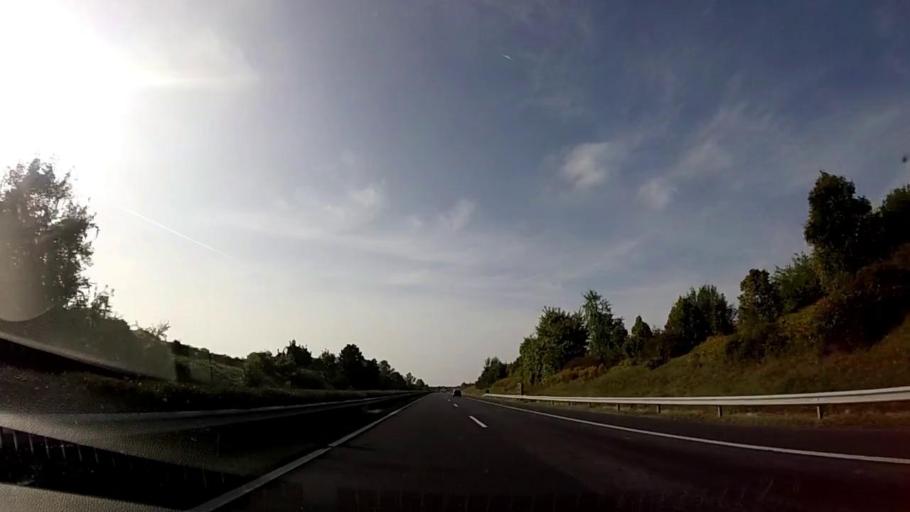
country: HU
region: Fejer
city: Lepseny
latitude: 46.9766
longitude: 18.1729
